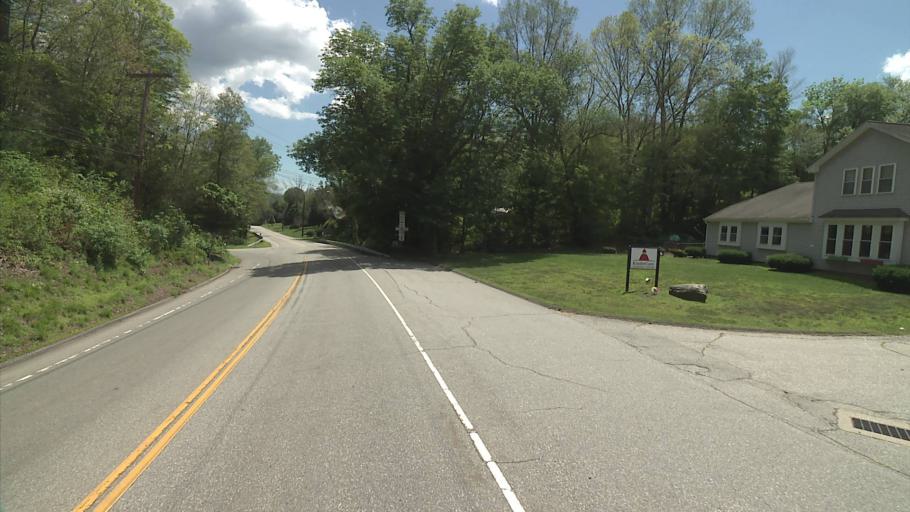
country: US
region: Connecticut
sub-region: Middlesex County
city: Moodus
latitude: 41.5031
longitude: -72.4744
